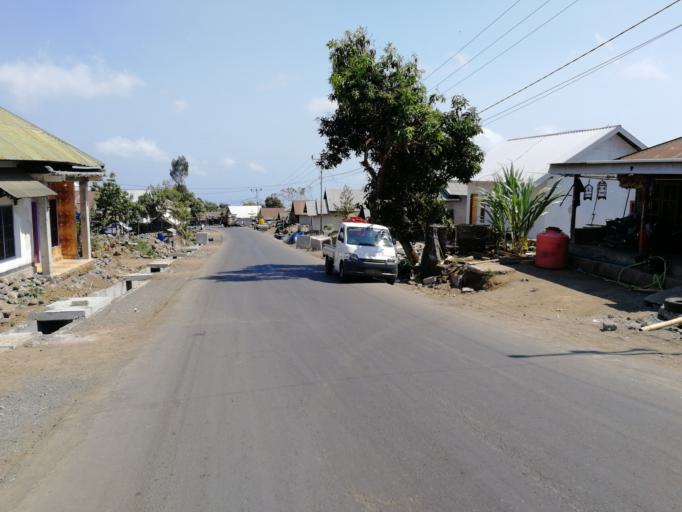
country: ID
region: West Nusa Tenggara
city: Lelongken
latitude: -8.3355
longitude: 116.4997
